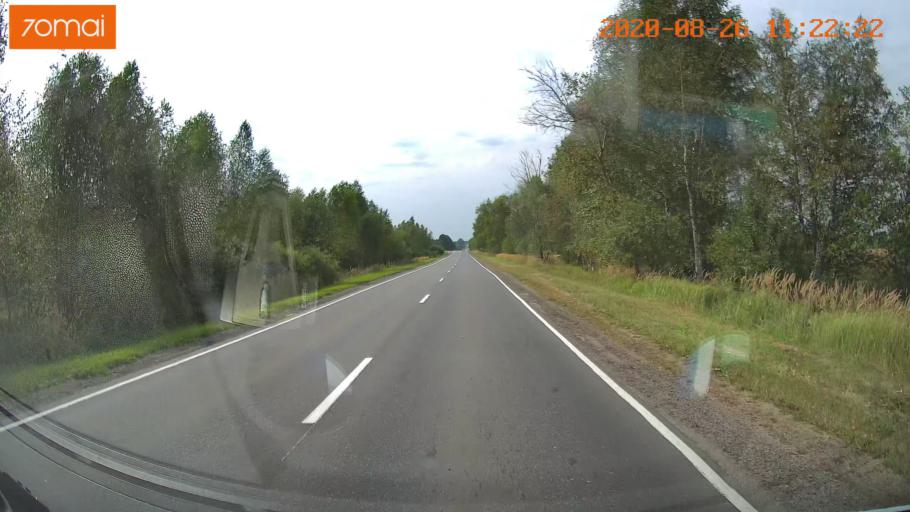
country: RU
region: Rjazan
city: Shilovo
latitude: 54.3648
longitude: 41.0285
